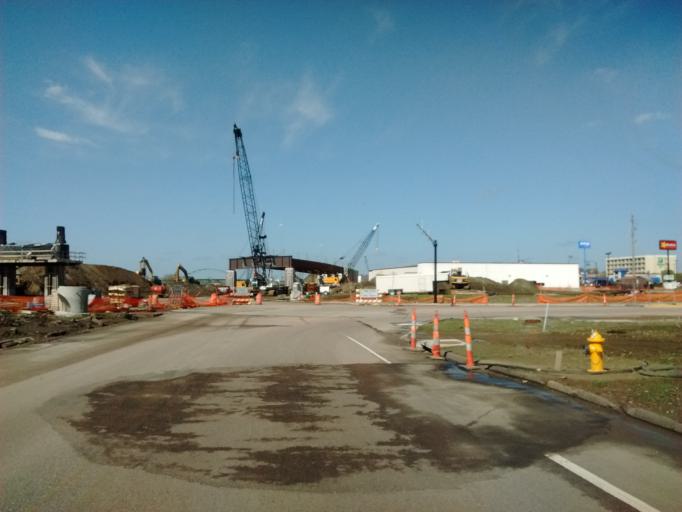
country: US
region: Iowa
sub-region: Woodbury County
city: Sioux City
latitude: 42.4888
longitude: -96.3973
